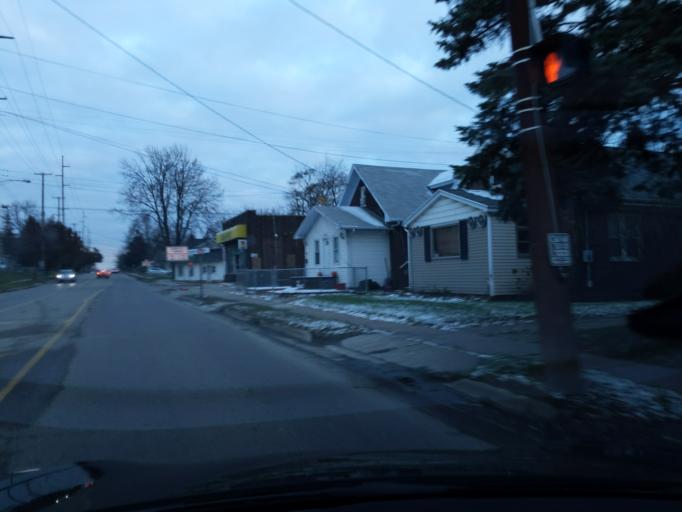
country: US
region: Michigan
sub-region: Ingham County
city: Lansing
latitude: 42.7557
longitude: -84.5381
